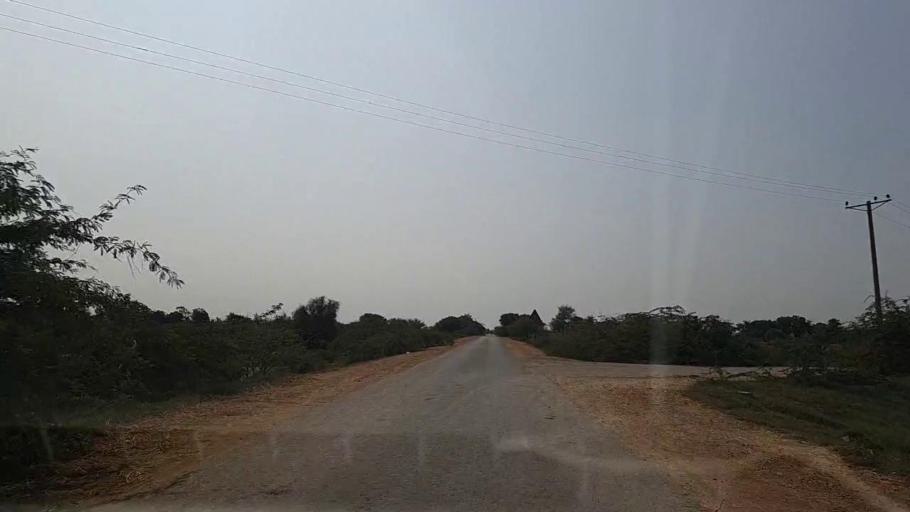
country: PK
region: Sindh
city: Chuhar Jamali
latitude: 24.2750
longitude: 67.9155
